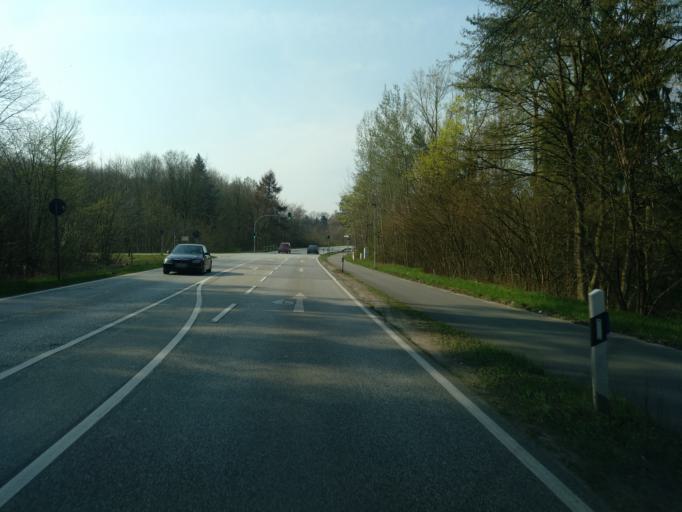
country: DE
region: Schleswig-Holstein
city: Ratekau
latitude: 53.8947
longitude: 10.7529
